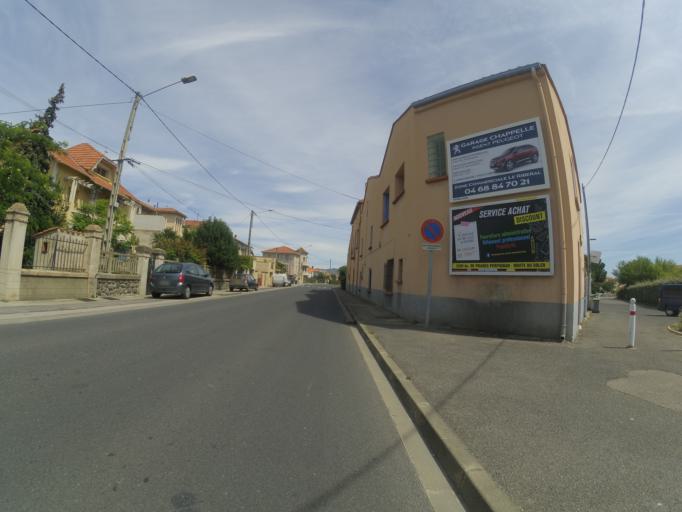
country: FR
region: Languedoc-Roussillon
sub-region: Departement des Pyrenees-Orientales
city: Ille-sur-Tet
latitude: 42.6745
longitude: 2.6256
